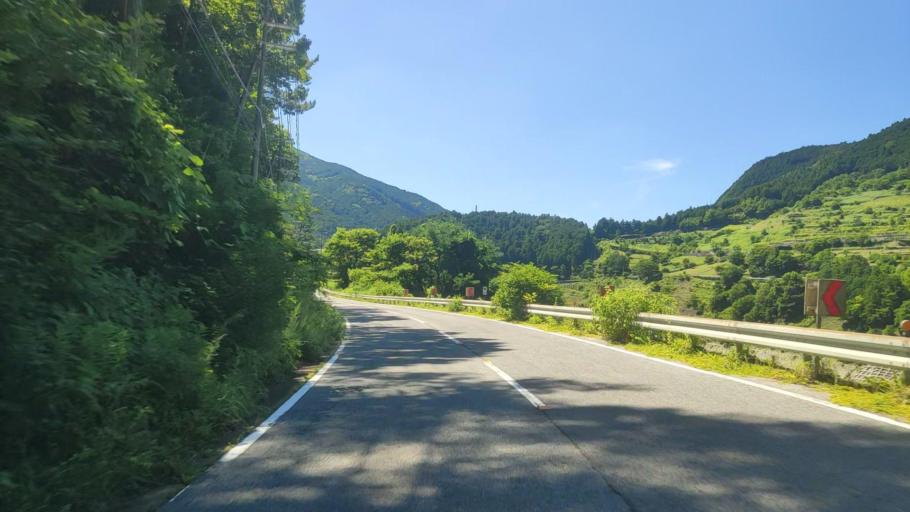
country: JP
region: Nara
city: Yoshino-cho
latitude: 34.3312
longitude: 135.9698
